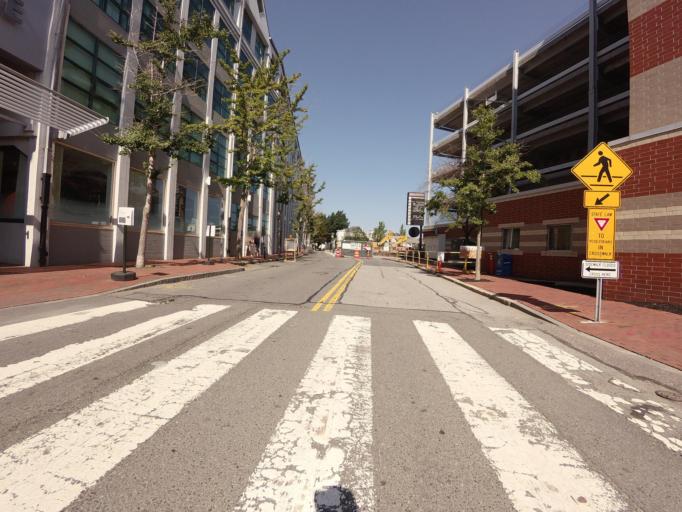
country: US
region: Massachusetts
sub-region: Middlesex County
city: Cambridge
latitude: 42.3673
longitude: -71.0897
